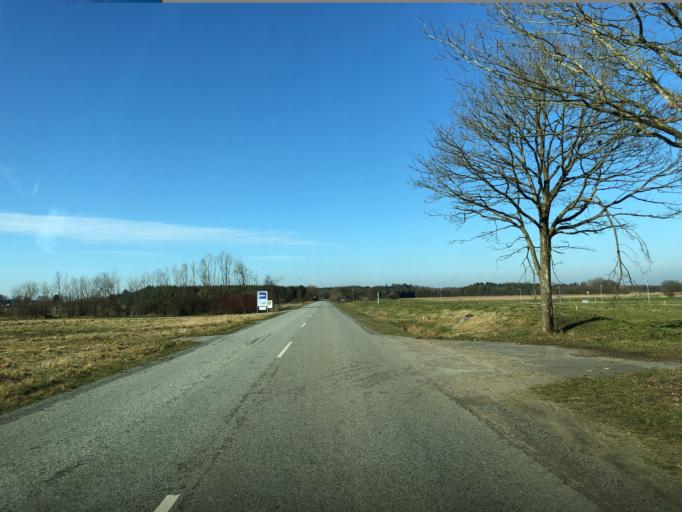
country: DK
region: Central Jutland
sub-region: Ikast-Brande Kommune
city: Bording Kirkeby
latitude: 56.1510
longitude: 9.2699
